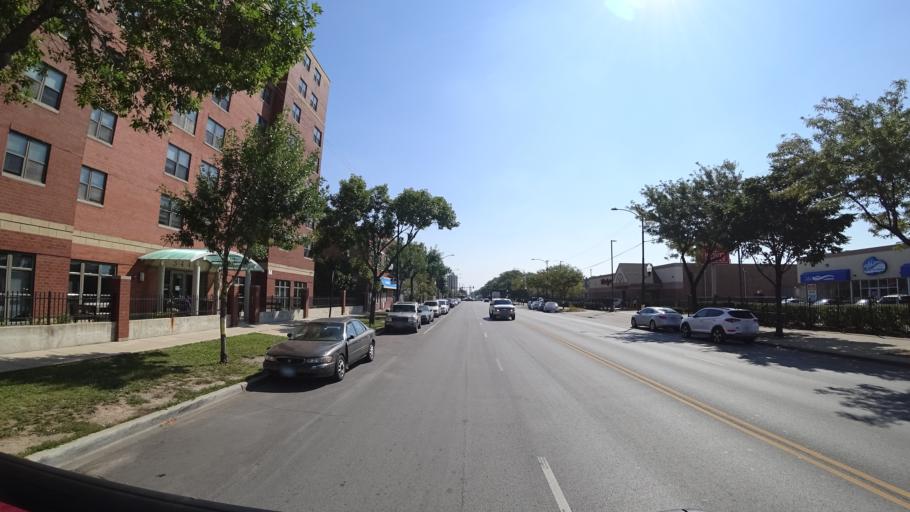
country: US
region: Illinois
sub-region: Cook County
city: Cicero
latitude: 41.8664
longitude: -87.7125
